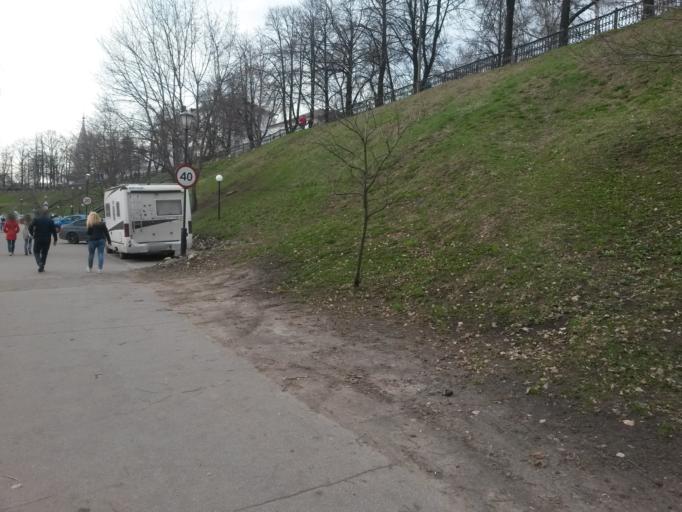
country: RU
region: Jaroslavl
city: Yaroslavl
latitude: 57.6214
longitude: 39.9014
